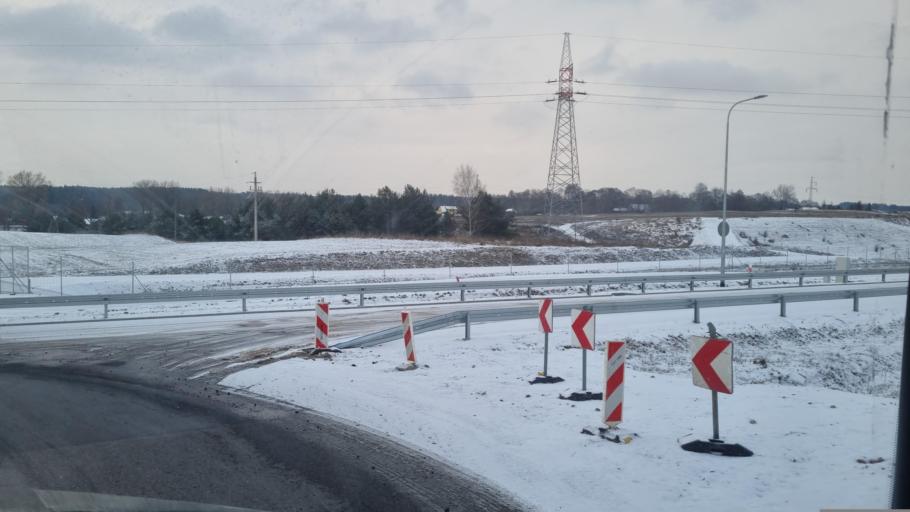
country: PL
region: Podlasie
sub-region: Suwalki
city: Suwalki
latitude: 54.1342
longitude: 22.9575
